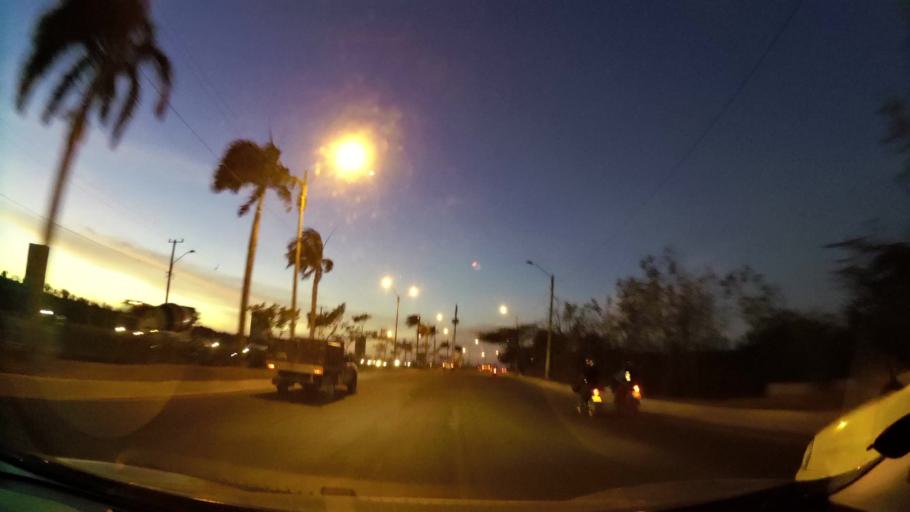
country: CO
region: Atlantico
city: Barranquilla
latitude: 10.9300
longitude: -74.8315
